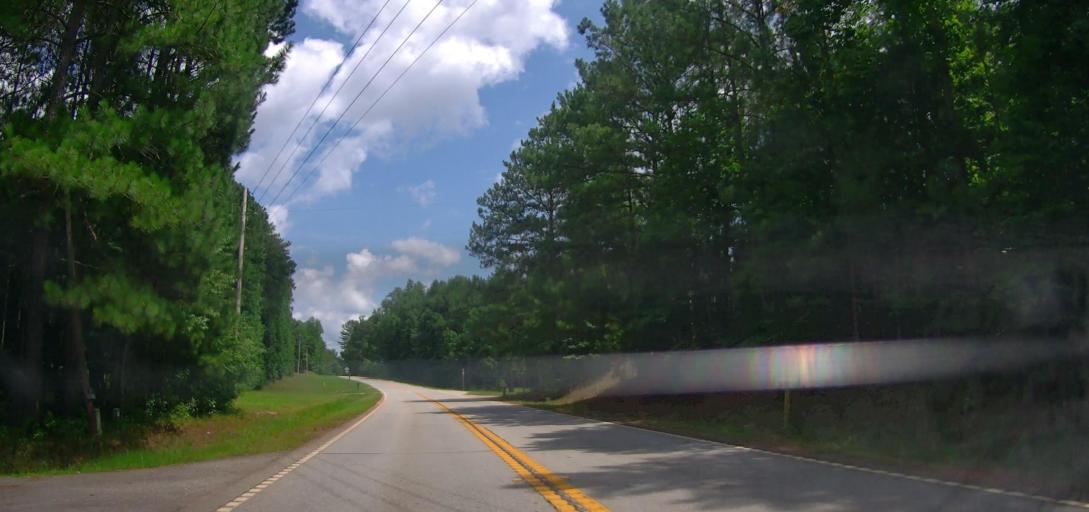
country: US
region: Georgia
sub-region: Heard County
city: Franklin
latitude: 33.3126
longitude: -85.1453
